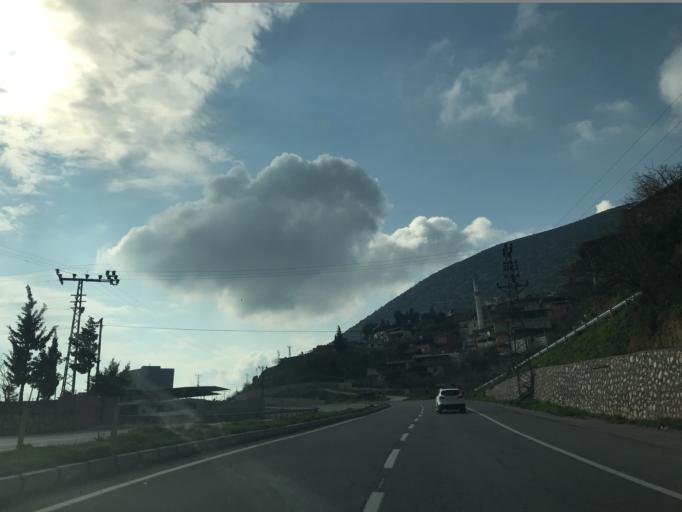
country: TR
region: Hatay
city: Belen
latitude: 36.4829
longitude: 36.2703
